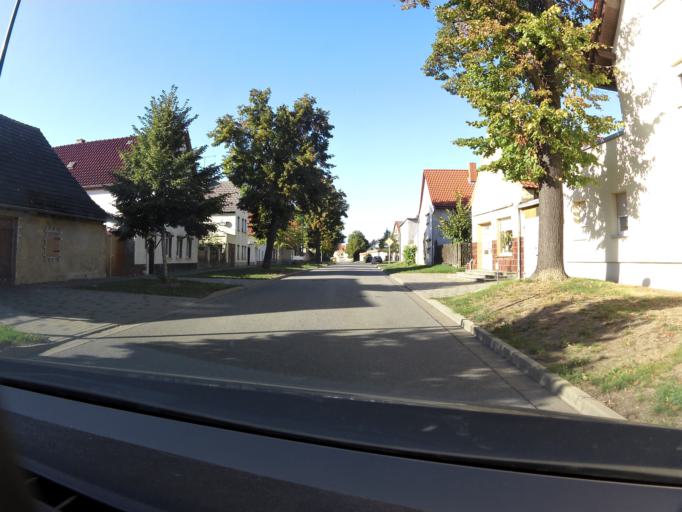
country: DE
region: Saxony-Anhalt
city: Hedersleben
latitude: 51.8600
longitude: 11.2517
